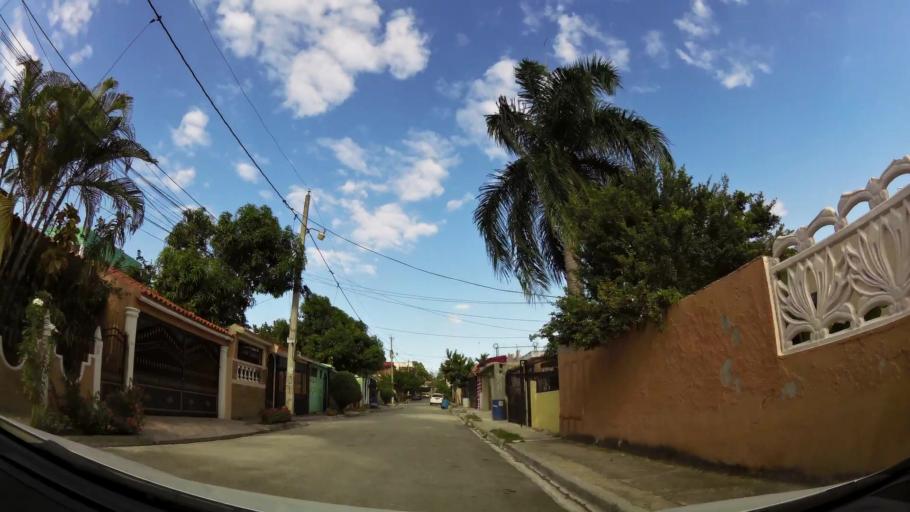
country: DO
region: Nacional
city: Ensanche Luperon
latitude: 18.5545
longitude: -69.8958
